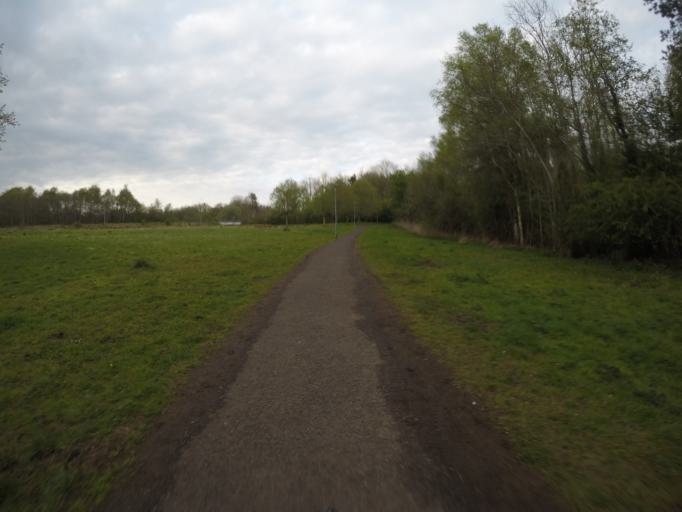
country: GB
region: Scotland
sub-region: North Ayrshire
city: Irvine
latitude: 55.6361
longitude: -4.6354
